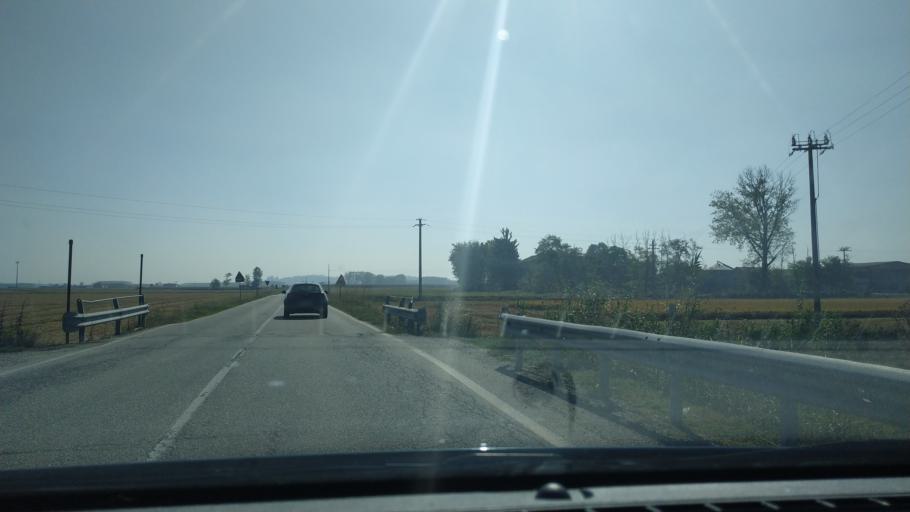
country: IT
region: Piedmont
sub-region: Provincia di Alessandria
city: Ticineto
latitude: 45.0876
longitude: 8.5510
